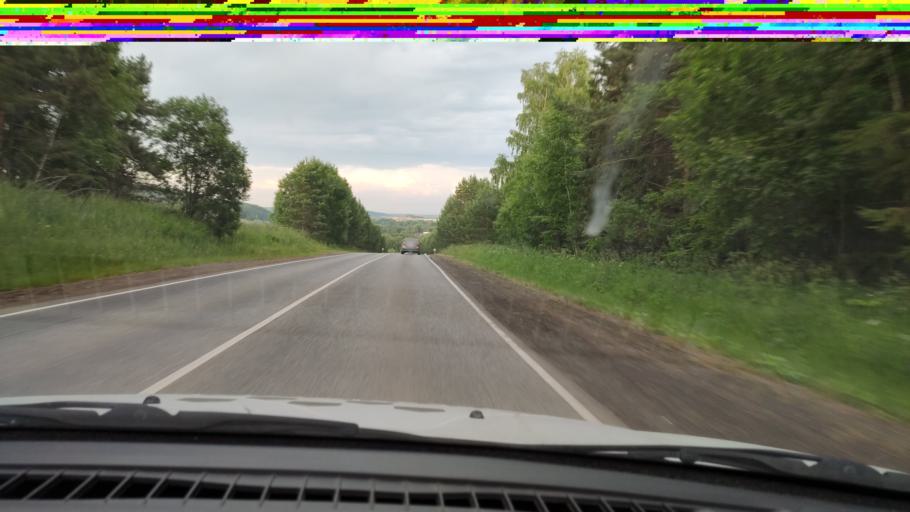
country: RU
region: Perm
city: Kukushtan
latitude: 57.4818
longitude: 56.5954
